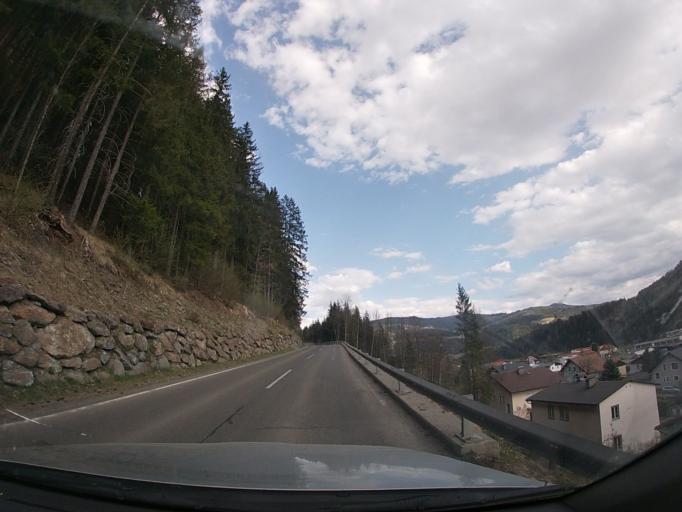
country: AT
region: Styria
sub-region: Politischer Bezirk Murau
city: Murau
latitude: 47.1141
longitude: 14.1807
